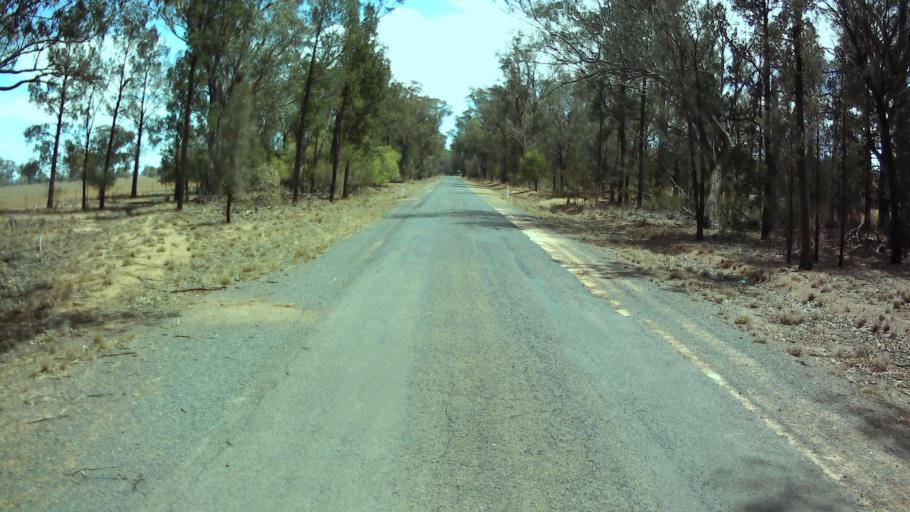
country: AU
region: New South Wales
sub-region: Weddin
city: Grenfell
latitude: -33.6478
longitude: 148.1928
